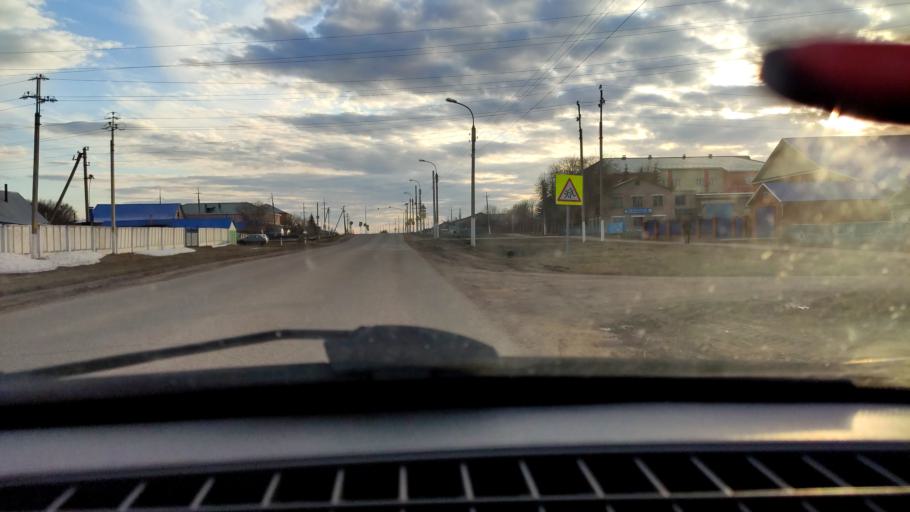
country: RU
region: Bashkortostan
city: Tolbazy
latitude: 54.0089
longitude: 55.8795
